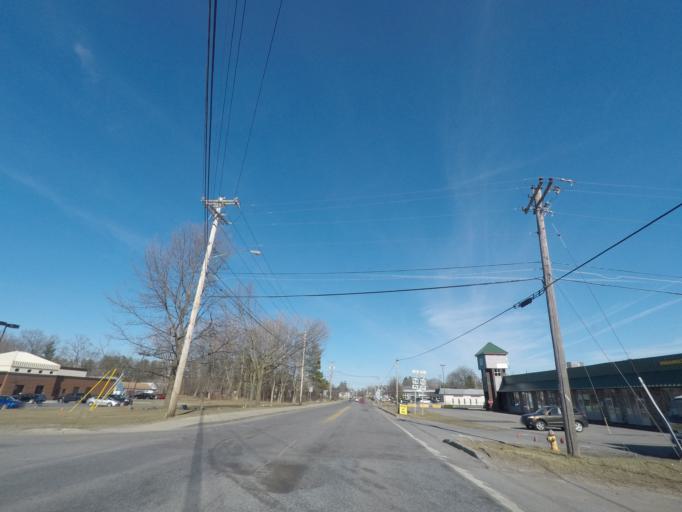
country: US
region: New York
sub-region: Saratoga County
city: Saratoga Springs
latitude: 43.0792
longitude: -73.8063
